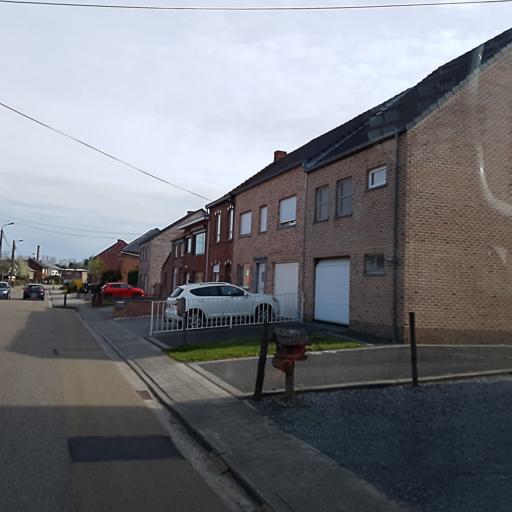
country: BE
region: Flanders
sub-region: Provincie Vlaams-Brabant
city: Aarschot
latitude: 51.0070
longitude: 4.8340
